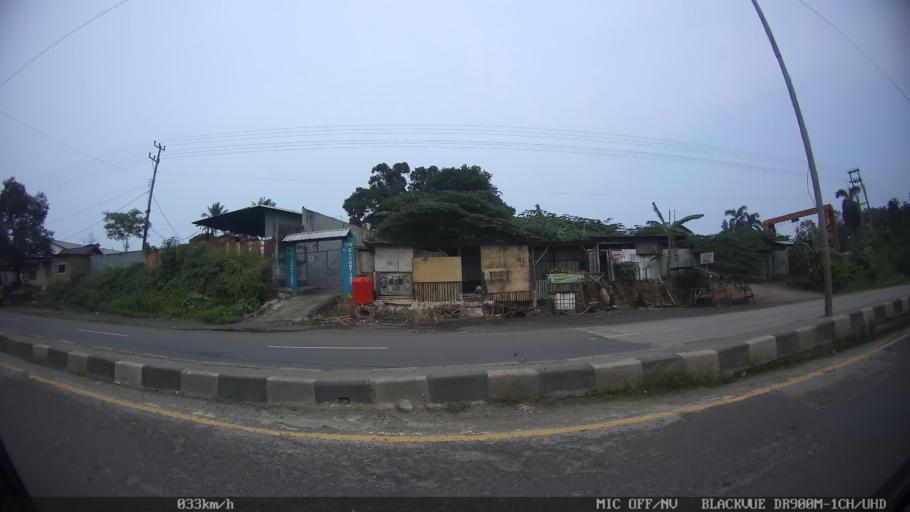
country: ID
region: Lampung
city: Bandarlampung
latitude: -5.4270
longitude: 105.2964
